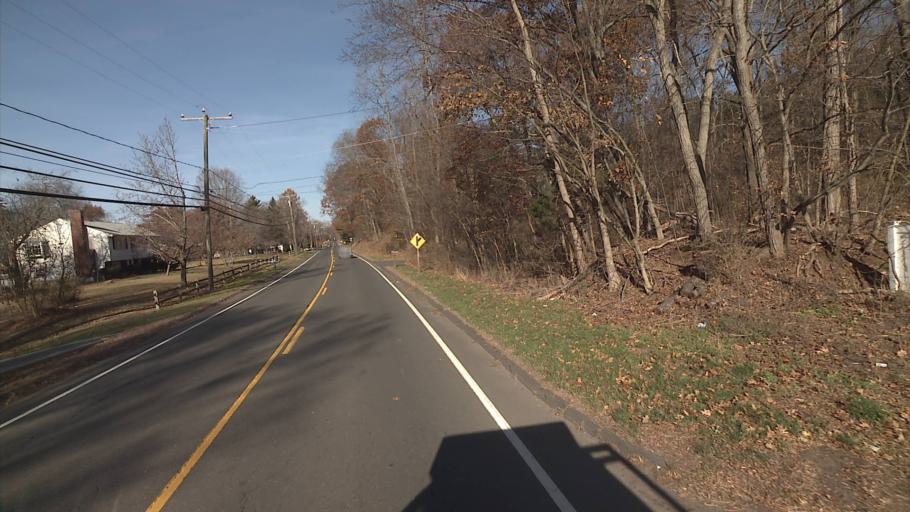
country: US
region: Connecticut
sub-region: Middlesex County
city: Cromwell
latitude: 41.6164
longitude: -72.5991
